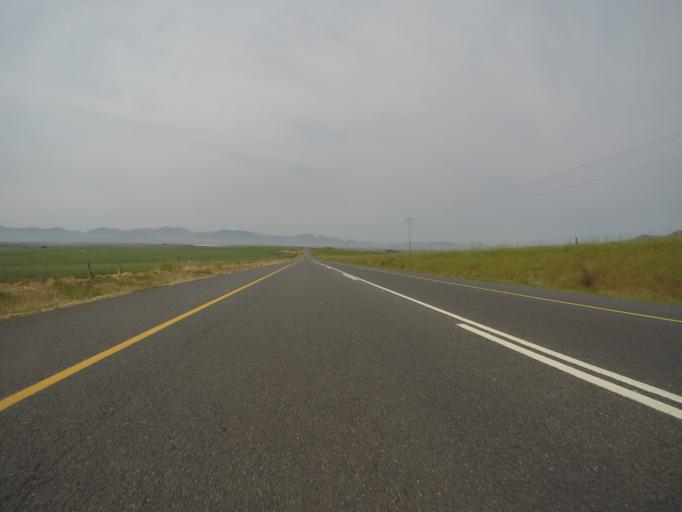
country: ZA
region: Western Cape
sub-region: West Coast District Municipality
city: Malmesbury
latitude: -33.5458
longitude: 18.8639
